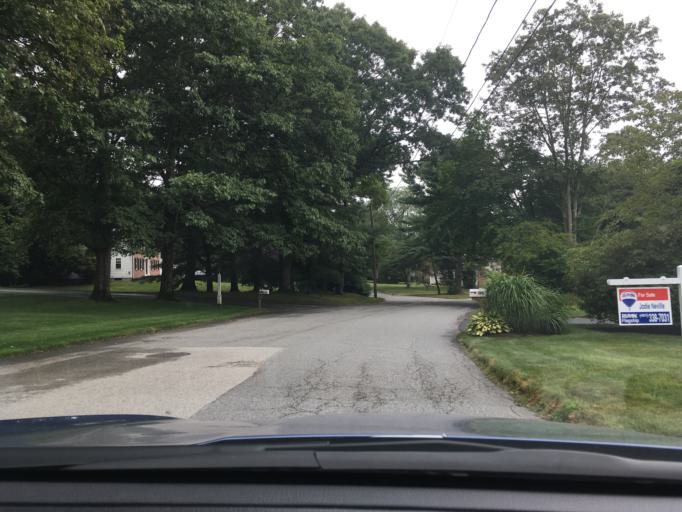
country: US
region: Rhode Island
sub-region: Kent County
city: East Greenwich
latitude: 41.6536
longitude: -71.4866
